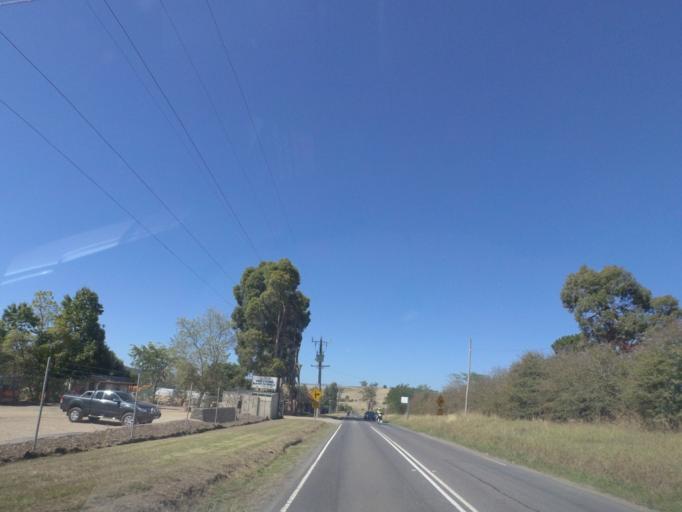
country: AU
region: Victoria
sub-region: Yarra Ranges
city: Chirnside Park
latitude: -37.7303
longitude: 145.2870
